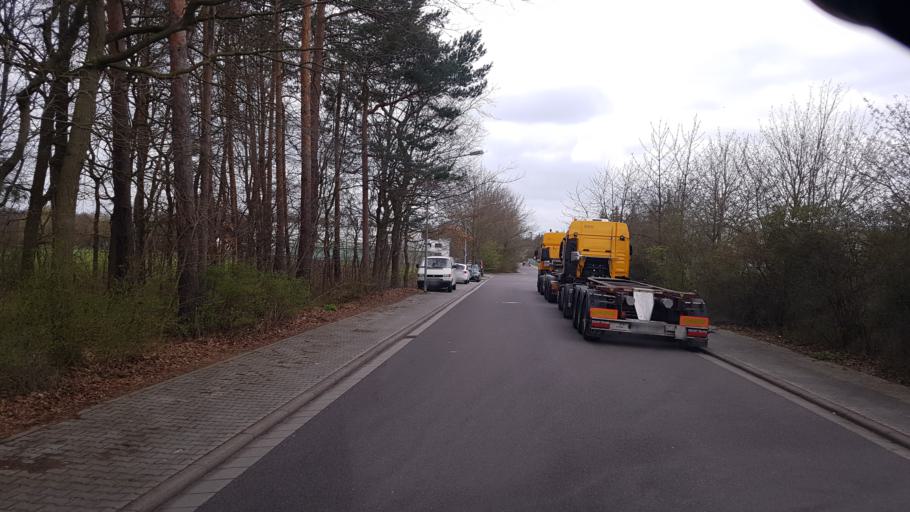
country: DE
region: Brandenburg
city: Lauchhammer
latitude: 51.4707
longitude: 13.8086
